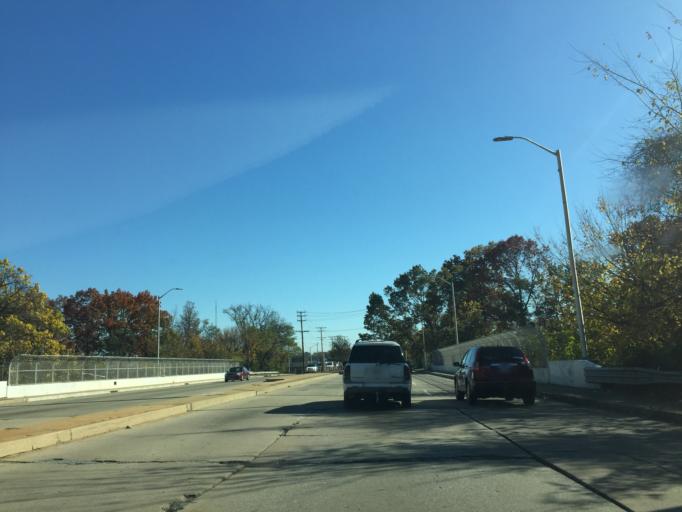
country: US
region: Maryland
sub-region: Baltimore County
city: Lansdowne
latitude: 39.2504
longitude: -76.6431
